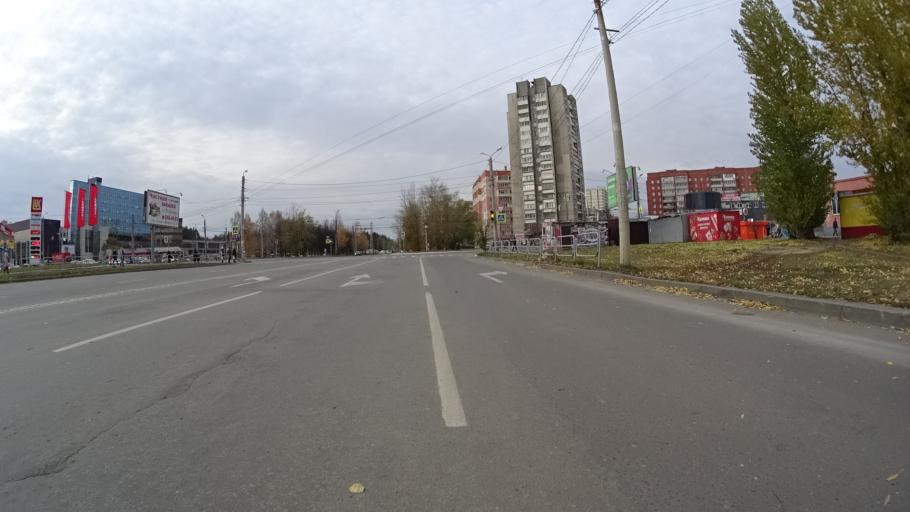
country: RU
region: Chelyabinsk
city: Roshchino
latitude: 55.1933
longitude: 61.3023
